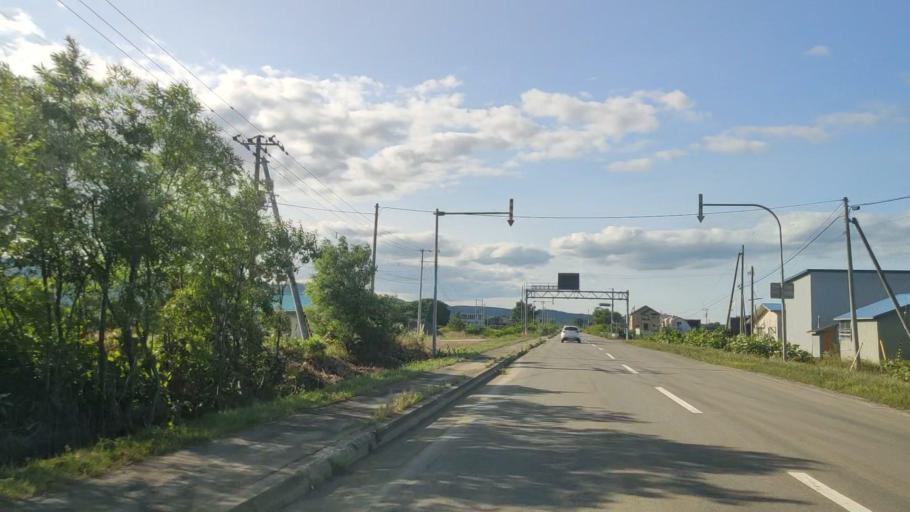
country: JP
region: Hokkaido
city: Makubetsu
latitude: 44.8219
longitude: 142.0664
